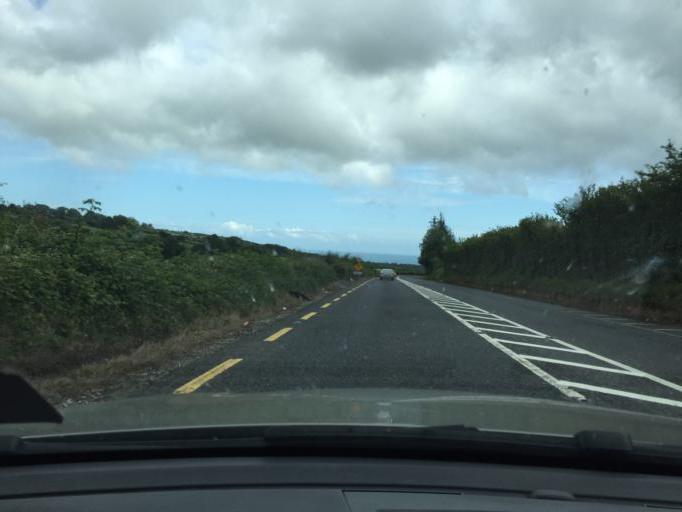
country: IE
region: Munster
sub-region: Waterford
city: Dungarvan
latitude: 52.1183
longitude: -7.5603
